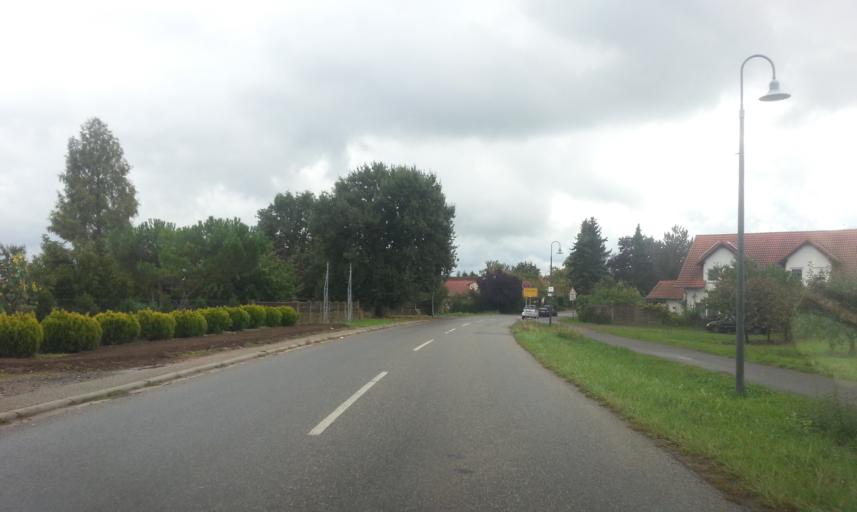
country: DE
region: Rheinland-Pfalz
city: Freinsheim
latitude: 49.5104
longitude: 8.2051
